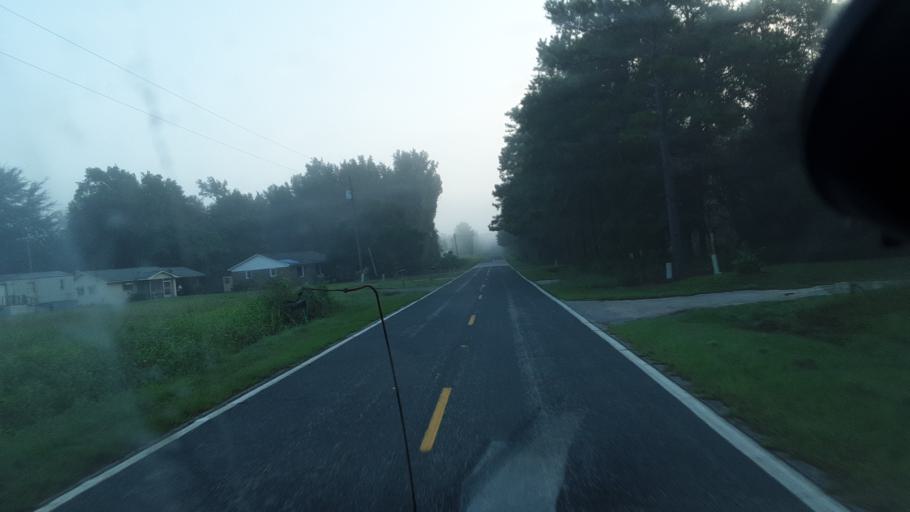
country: US
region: South Carolina
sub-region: Clarendon County
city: Manning
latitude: 33.7399
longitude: -80.0812
